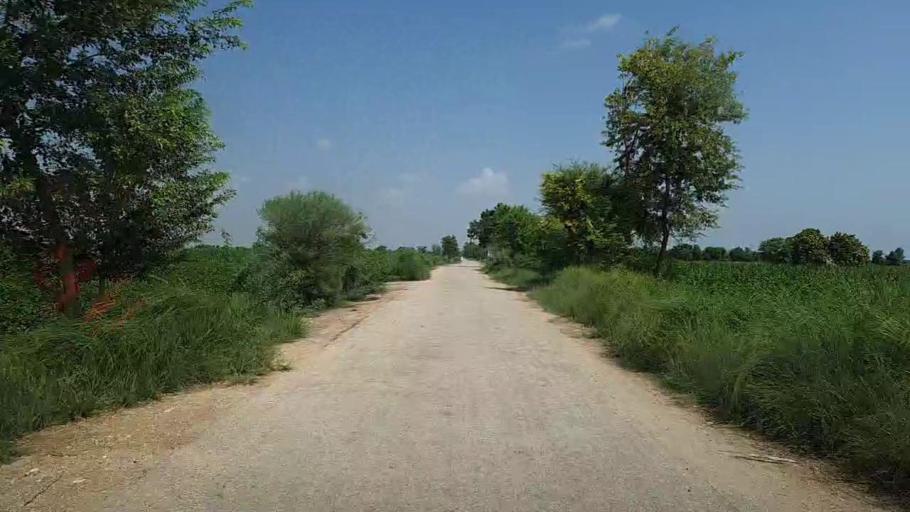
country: PK
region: Sindh
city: Bhiria
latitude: 26.8740
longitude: 68.2506
